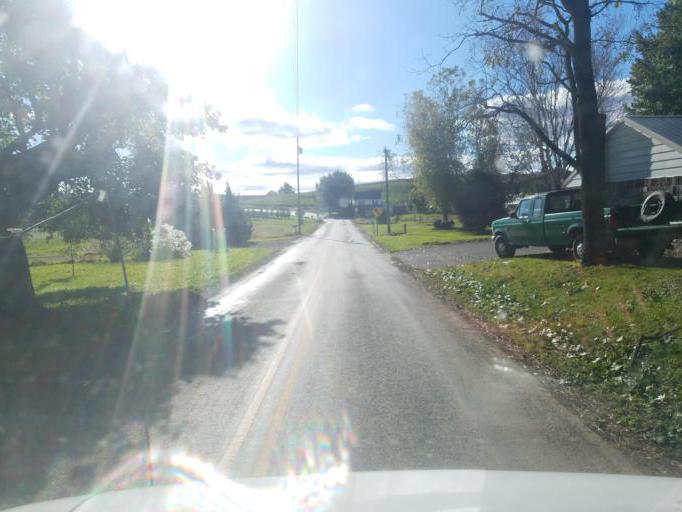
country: US
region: Pennsylvania
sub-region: Franklin County
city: Guilford Siding
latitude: 39.8105
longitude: -77.6209
